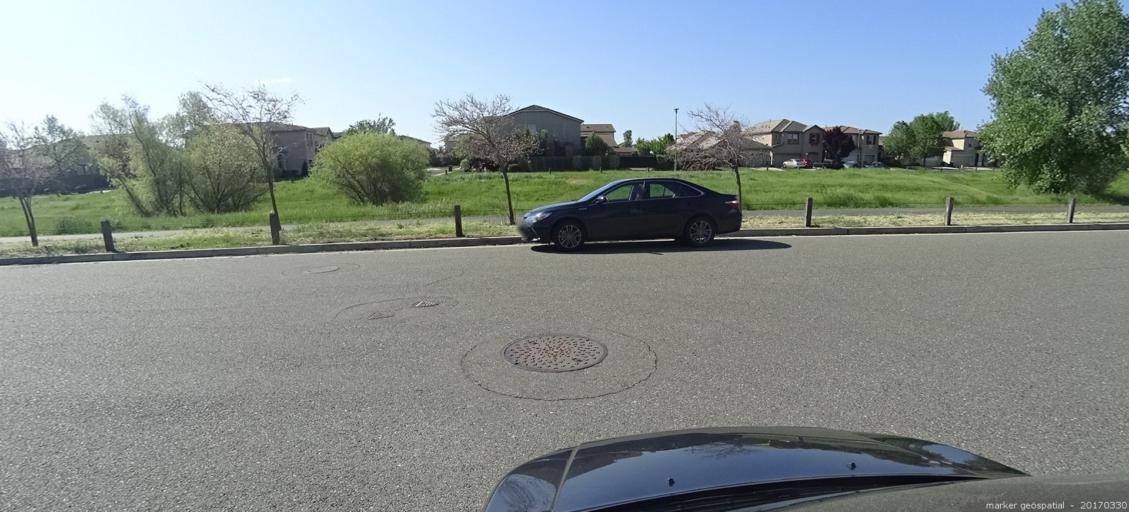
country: US
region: California
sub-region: Sacramento County
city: Laguna
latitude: 38.4435
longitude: -121.4122
